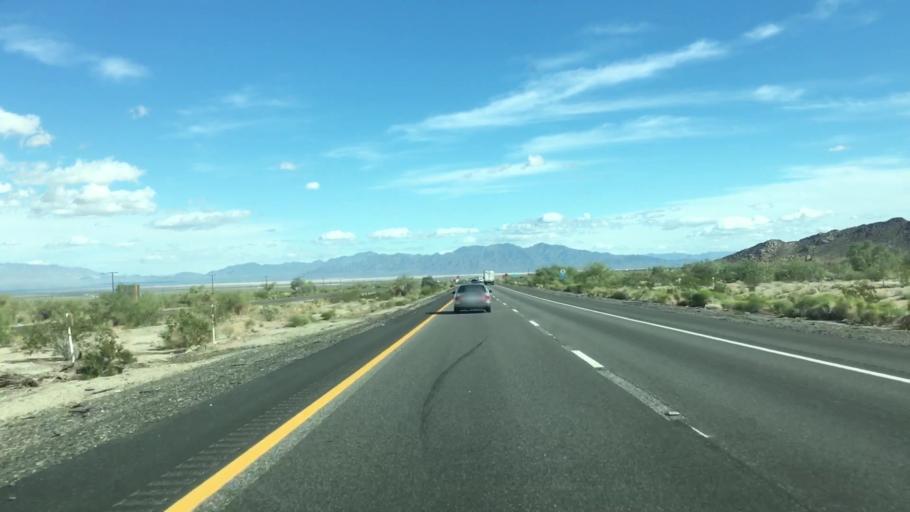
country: US
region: California
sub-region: Imperial County
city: Niland
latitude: 33.7081
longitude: -115.4251
